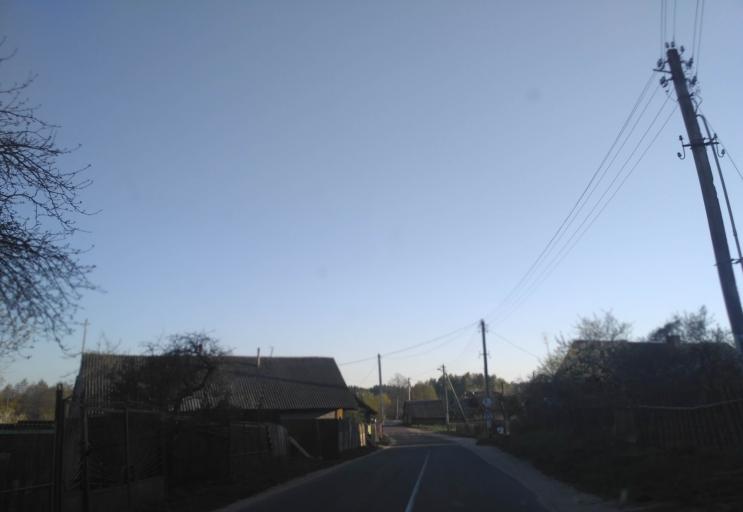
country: BY
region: Minsk
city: Radashkovichy
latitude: 54.1363
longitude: 27.2056
